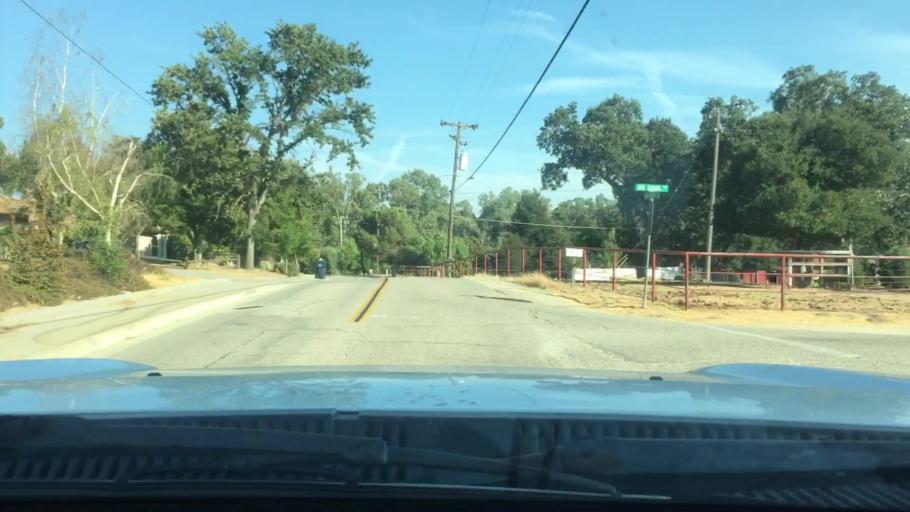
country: US
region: California
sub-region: San Luis Obispo County
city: Atascadero
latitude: 35.4618
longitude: -120.6742
